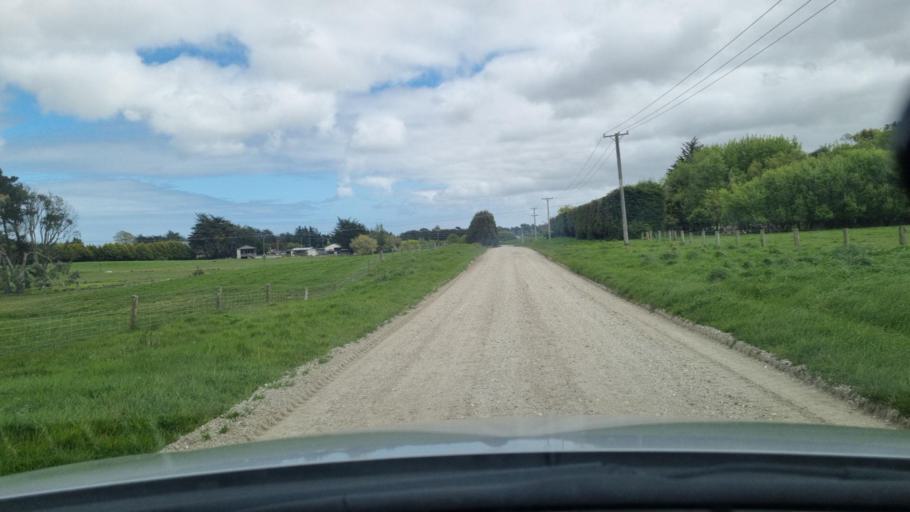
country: NZ
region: Southland
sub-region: Invercargill City
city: Invercargill
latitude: -46.4433
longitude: 168.4048
